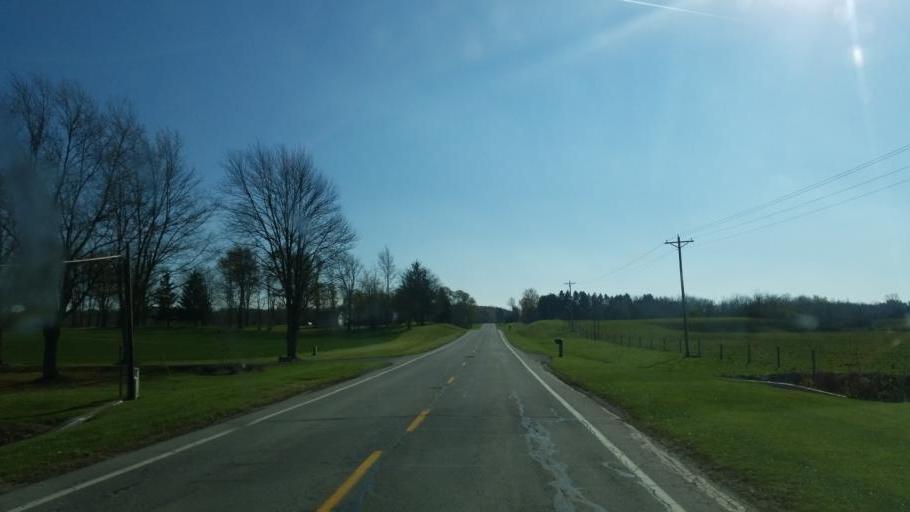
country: US
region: Ohio
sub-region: Lorain County
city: Wellington
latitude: 41.1458
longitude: -82.2181
